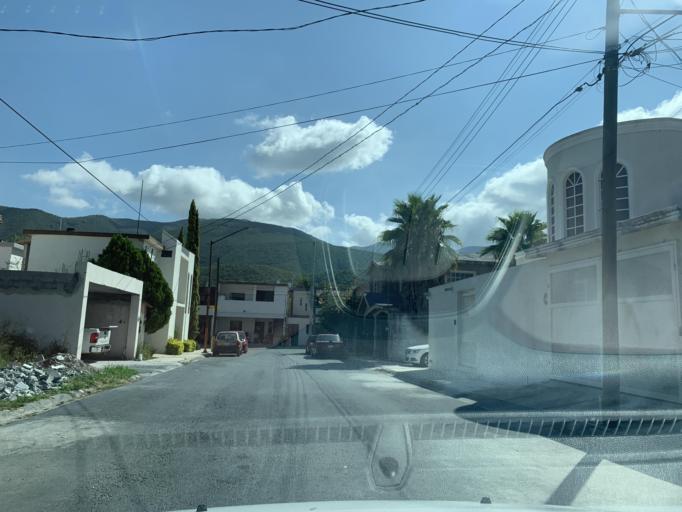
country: MX
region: Nuevo Leon
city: Santiago
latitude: 25.4006
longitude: -100.1294
